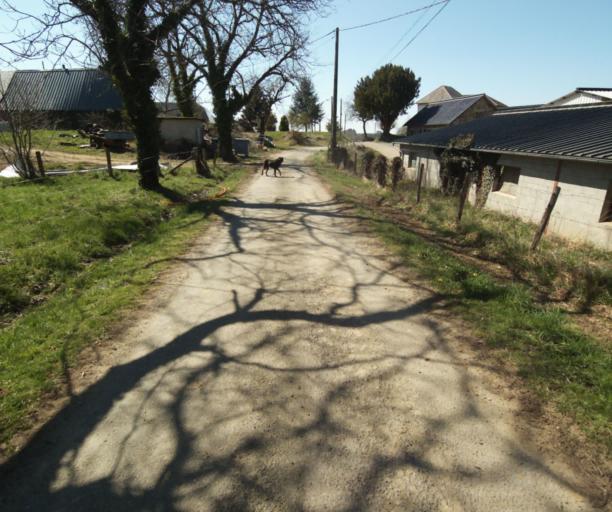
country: FR
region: Limousin
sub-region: Departement de la Correze
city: Saint-Clement
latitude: 45.3405
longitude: 1.7066
